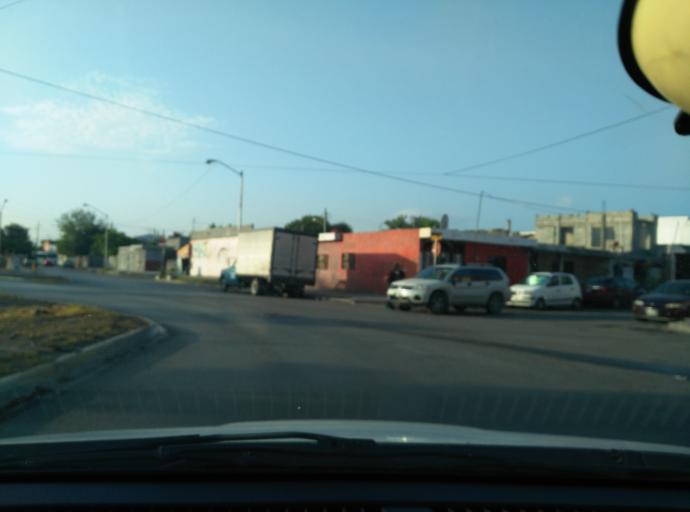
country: MX
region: Nuevo Leon
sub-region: San Nicolas de los Garza
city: San Nicolas de los Garza
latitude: 25.7575
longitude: -100.2495
